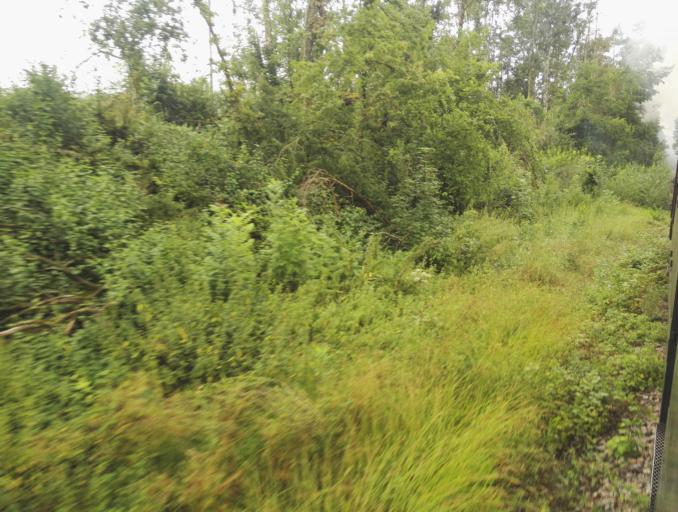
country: DE
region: Baden-Wuerttemberg
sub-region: Freiburg Region
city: Blumberg
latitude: 47.7936
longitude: 8.5168
